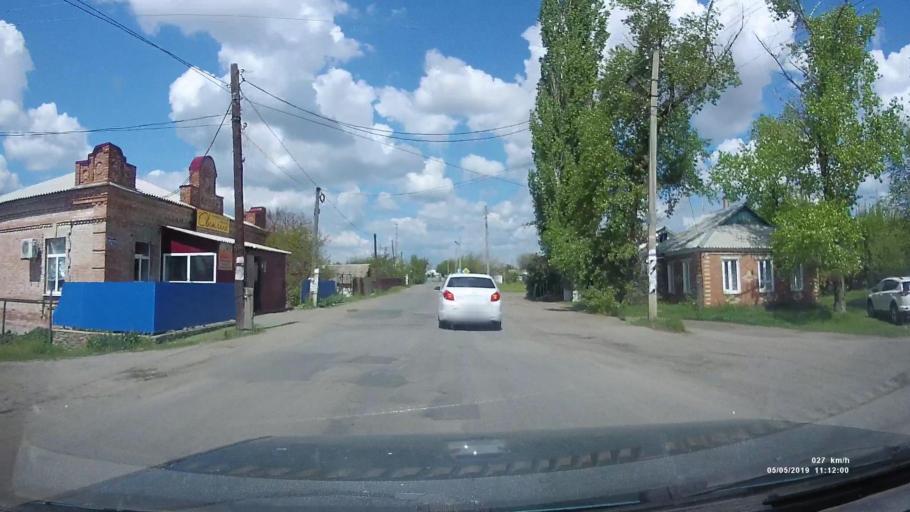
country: RU
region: Rostov
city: Ust'-Donetskiy
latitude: 47.7479
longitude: 40.9432
